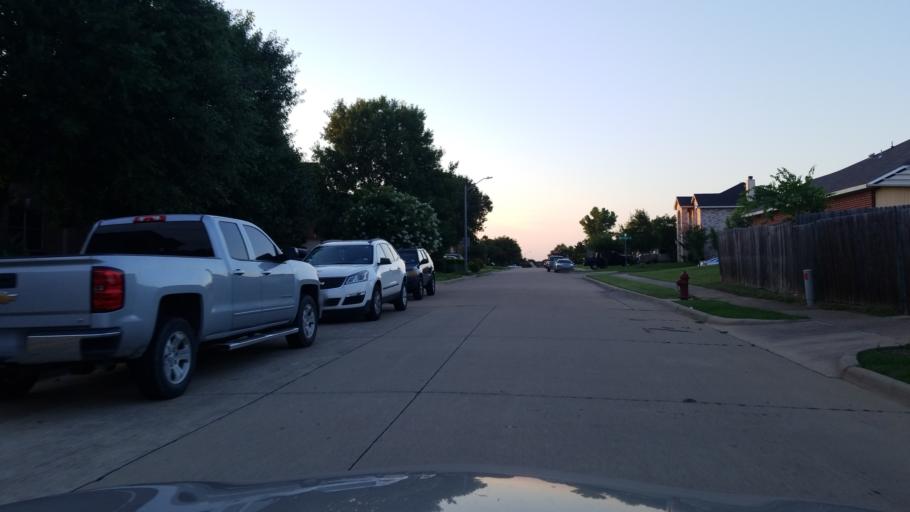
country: US
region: Texas
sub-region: Dallas County
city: Grand Prairie
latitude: 32.6867
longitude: -97.0416
